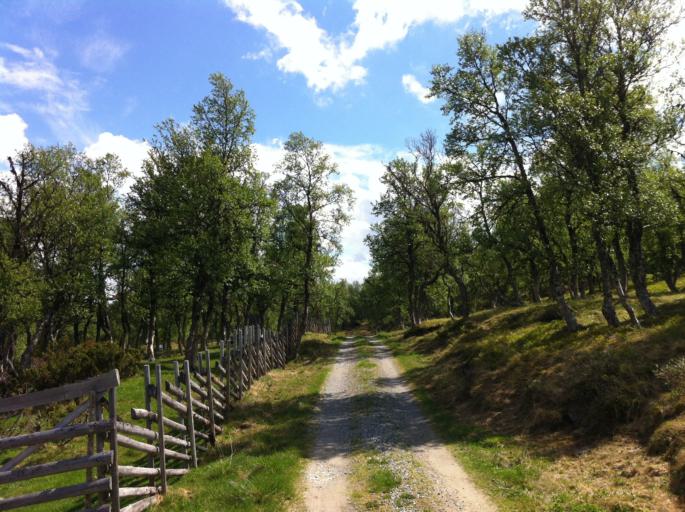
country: NO
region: Sor-Trondelag
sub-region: Tydal
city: Aas
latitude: 62.7088
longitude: 12.4743
